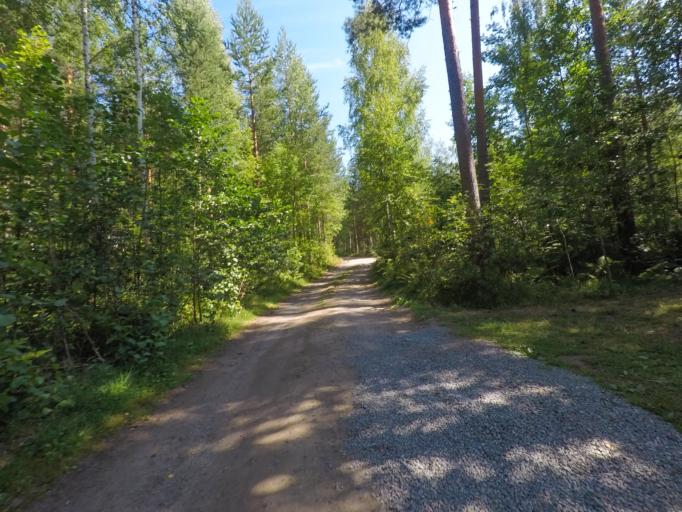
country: FI
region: Southern Savonia
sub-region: Mikkeli
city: Puumala
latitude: 61.4307
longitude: 28.0023
